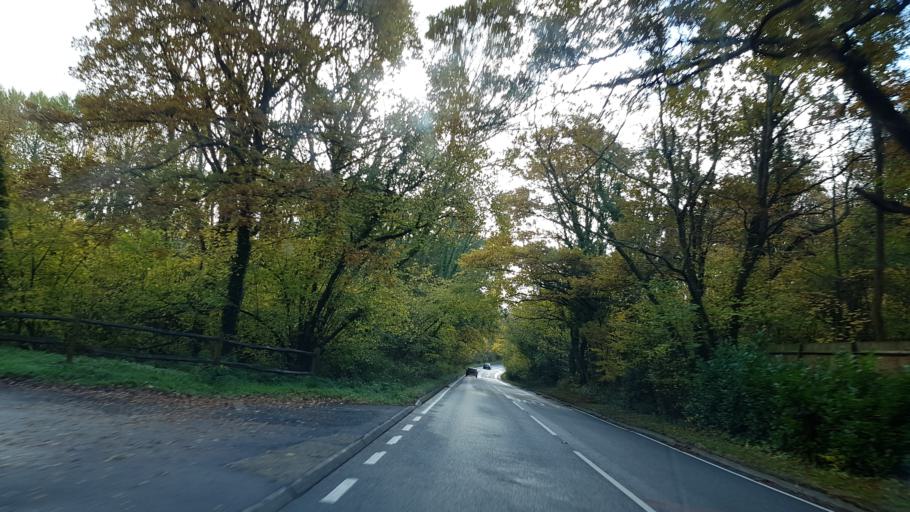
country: GB
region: England
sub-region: Surrey
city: Milford
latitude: 51.1304
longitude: -0.6727
